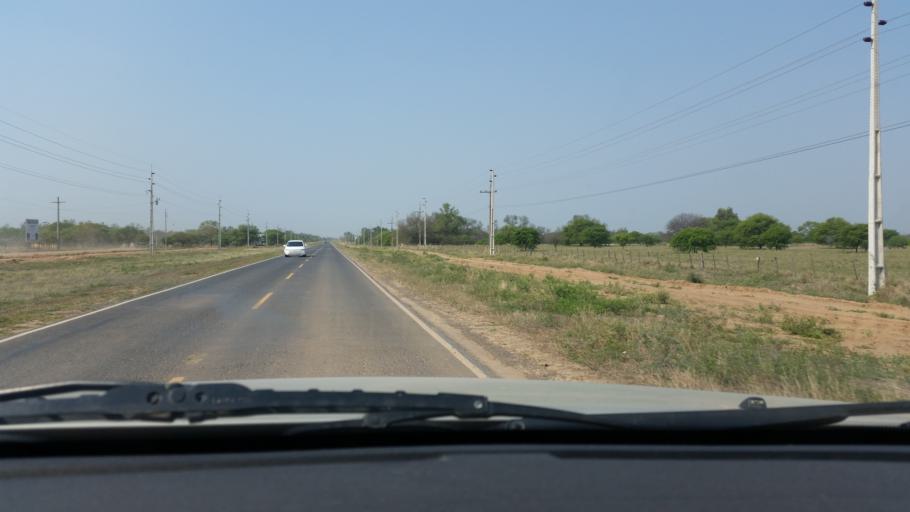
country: PY
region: Boqueron
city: Filadelfia
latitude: -22.3926
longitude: -60.0351
